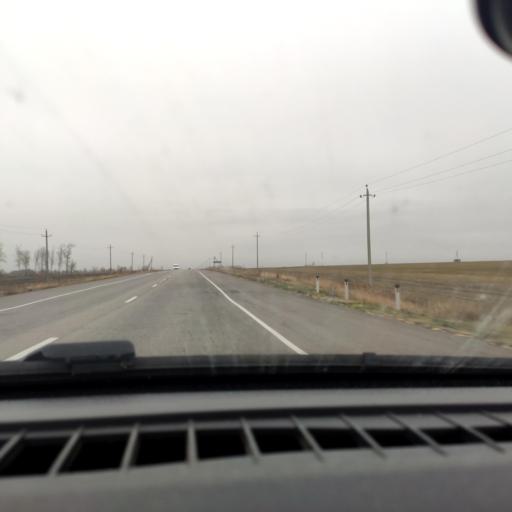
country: RU
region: Voronezj
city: Strelitsa
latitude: 51.5510
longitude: 38.9720
